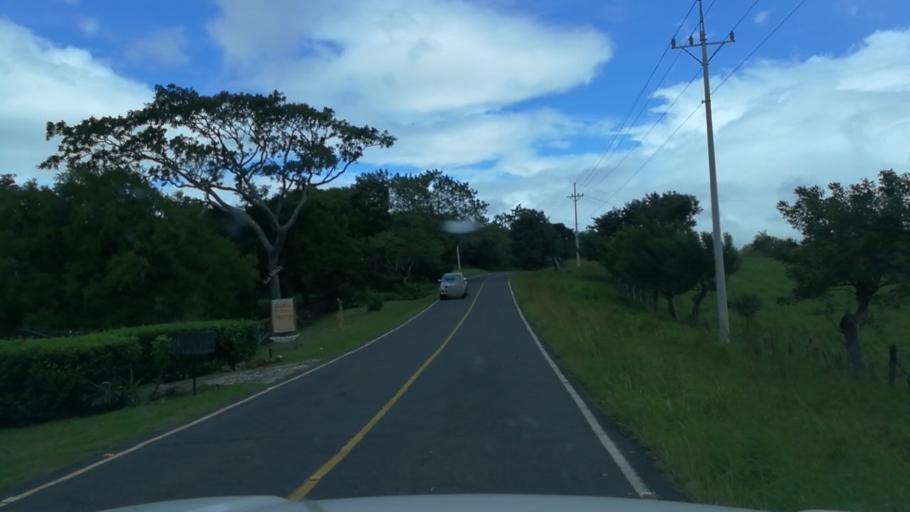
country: CR
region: Guanacaste
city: Fortuna
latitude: 10.6447
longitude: -85.2317
